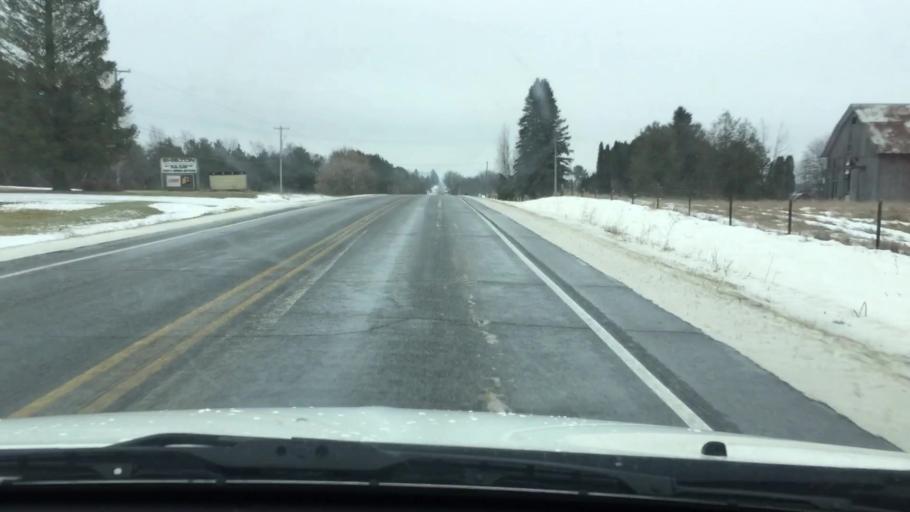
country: US
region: Michigan
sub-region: Wexford County
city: Cadillac
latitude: 44.0803
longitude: -85.4441
